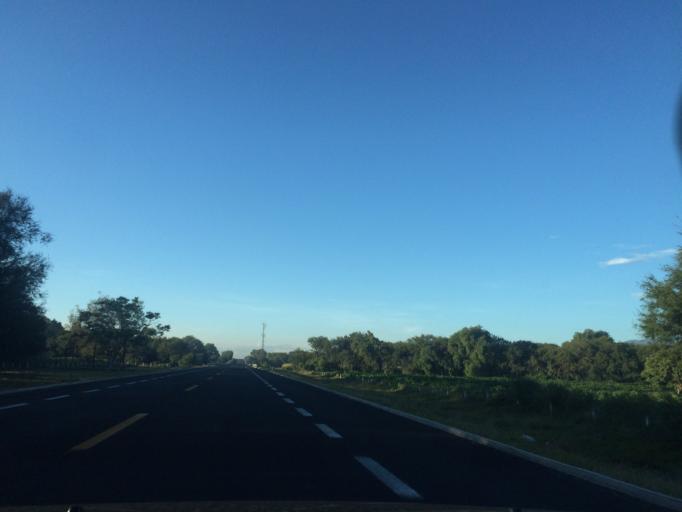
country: MX
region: Puebla
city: Santiago Miahuatlan
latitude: 18.5399
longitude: -97.4599
